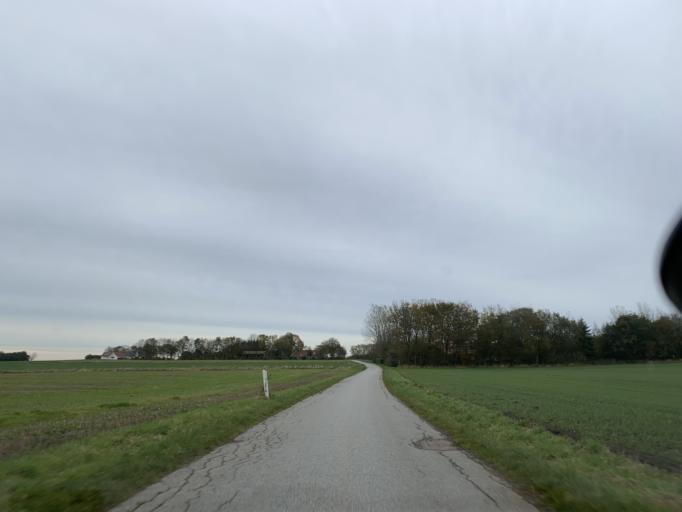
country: DK
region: Central Jutland
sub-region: Skanderborg Kommune
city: Ry
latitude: 56.1861
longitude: 9.7761
